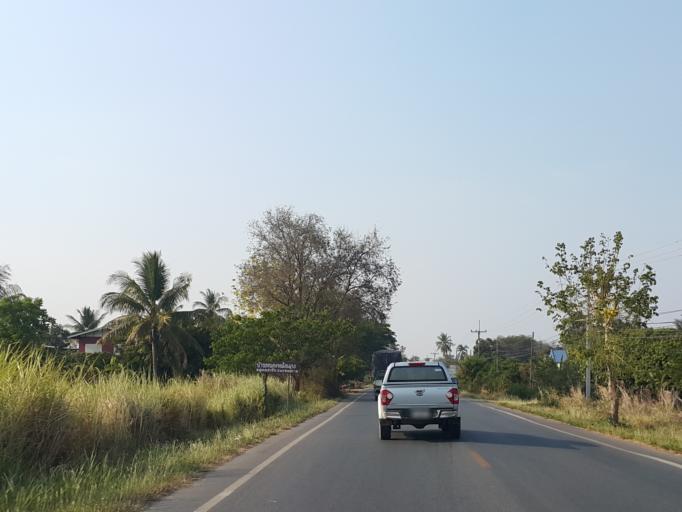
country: TH
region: Phitsanulok
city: Phrom Phiram
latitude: 16.9773
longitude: 100.2118
